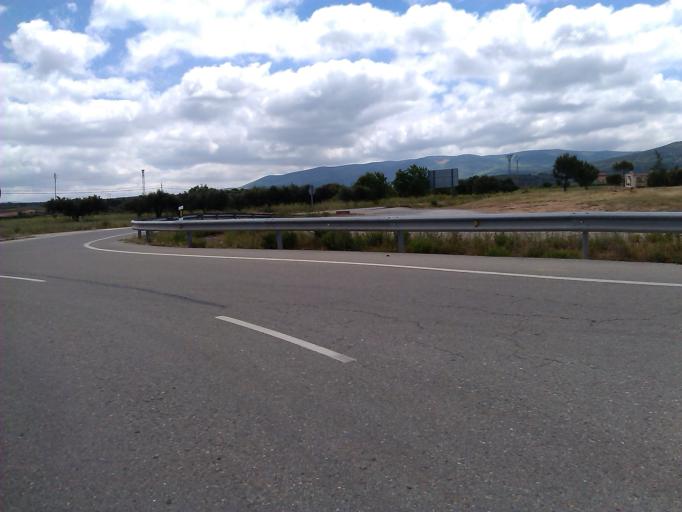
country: ES
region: La Rioja
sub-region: Provincia de La Rioja
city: Navarrete
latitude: 42.4205
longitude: -2.5904
